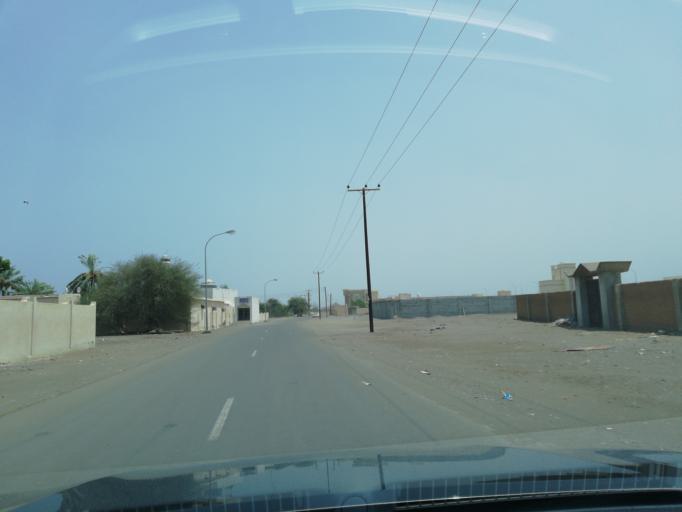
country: OM
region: Al Batinah
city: Al Liwa'
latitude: 24.6167
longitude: 56.5350
